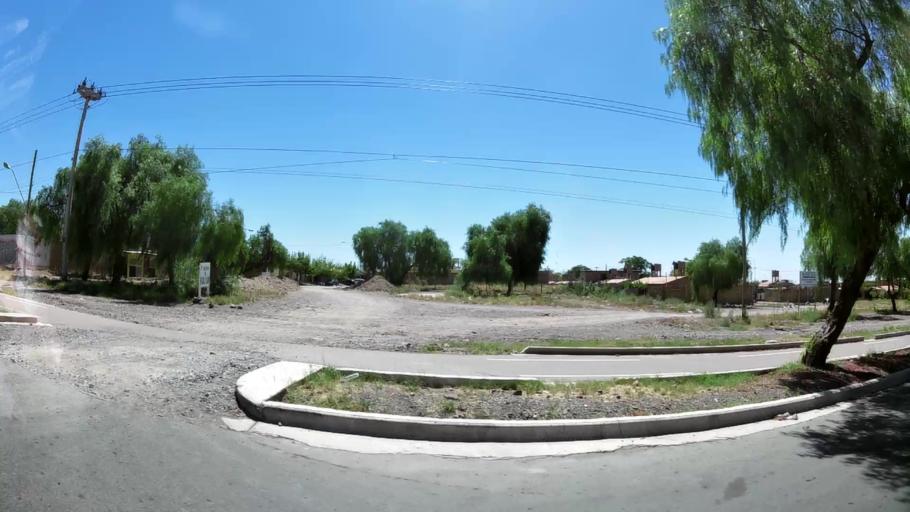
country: AR
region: Mendoza
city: Las Heras
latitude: -32.8534
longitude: -68.8651
